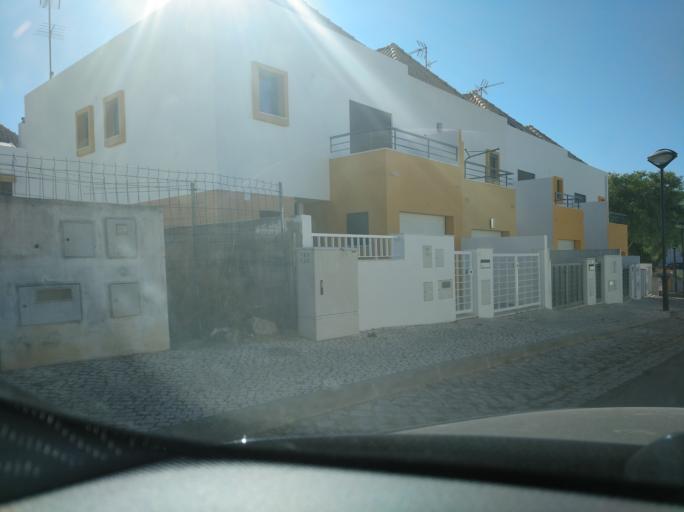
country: PT
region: Faro
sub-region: Vila Real de Santo Antonio
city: Monte Gordo
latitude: 37.1773
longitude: -7.5373
